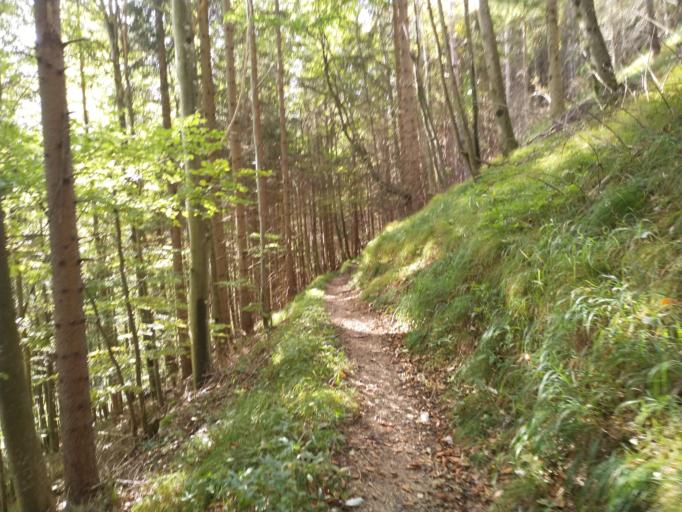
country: AT
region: Tyrol
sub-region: Politischer Bezirk Reutte
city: Vils
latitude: 47.5626
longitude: 10.6534
